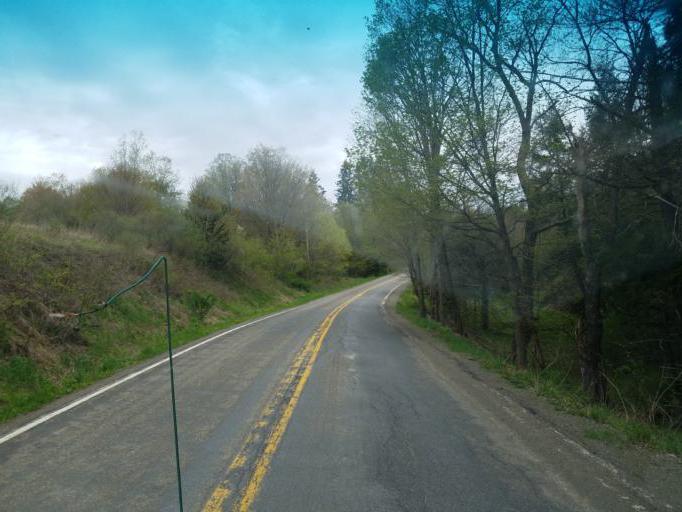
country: US
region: Pennsylvania
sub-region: Tioga County
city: Wellsboro
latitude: 41.6993
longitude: -77.4379
